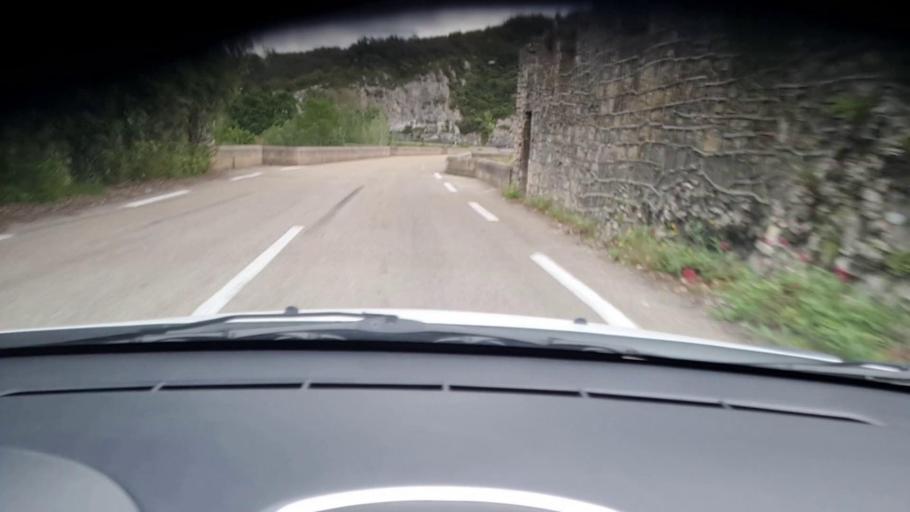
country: FR
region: Languedoc-Roussillon
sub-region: Departement du Gard
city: Blauzac
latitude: 43.9425
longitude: 4.3764
